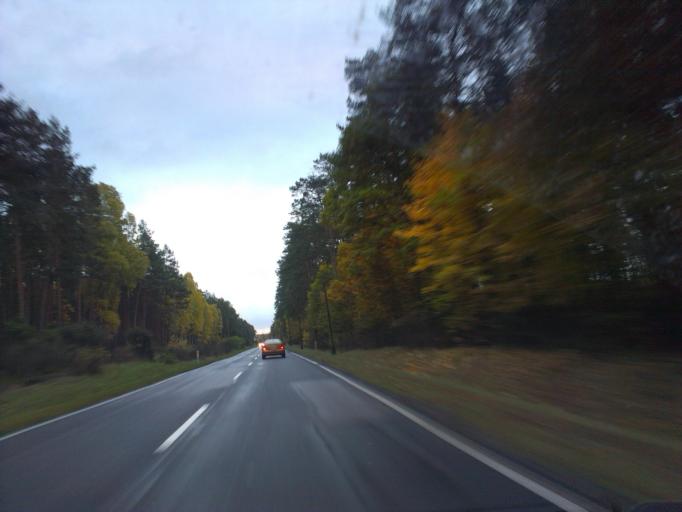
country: PL
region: Kujawsko-Pomorskie
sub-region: Powiat tucholski
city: Cekcyn
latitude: 53.5428
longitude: 17.9335
